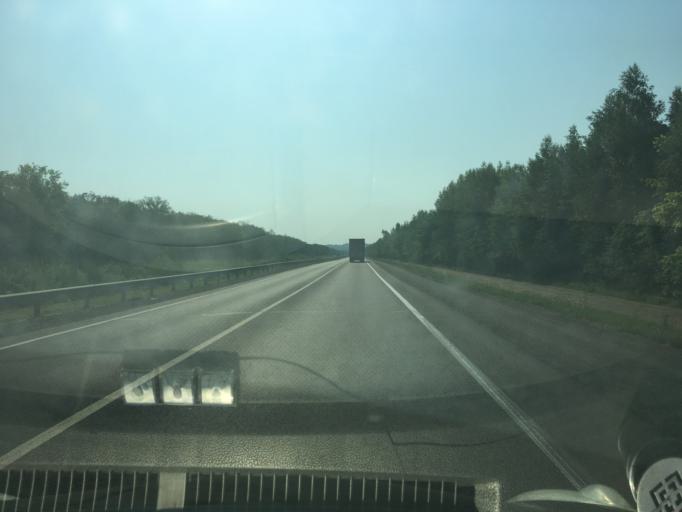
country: RU
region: Nizjnij Novgorod
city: Kstovo
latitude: 56.0877
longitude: 44.3402
